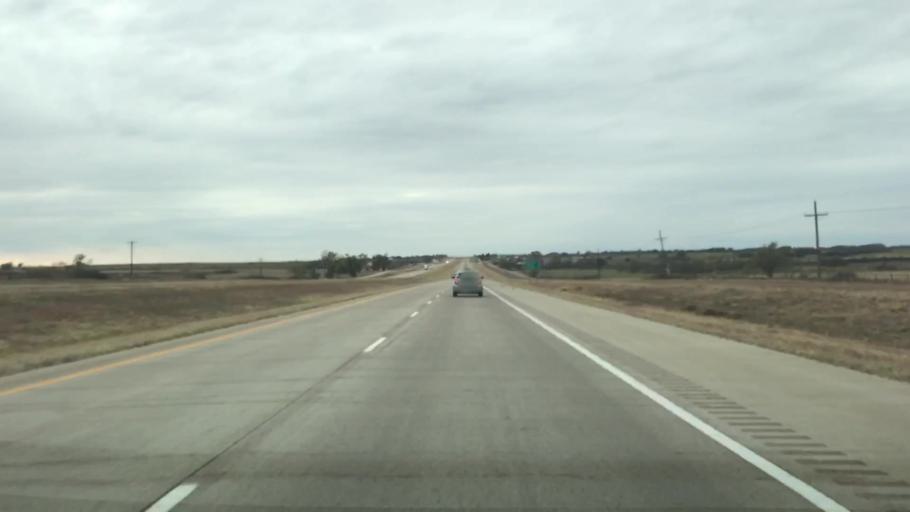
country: US
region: Texas
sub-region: Wheeler County
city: Shamrock
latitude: 35.2270
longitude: -100.1465
